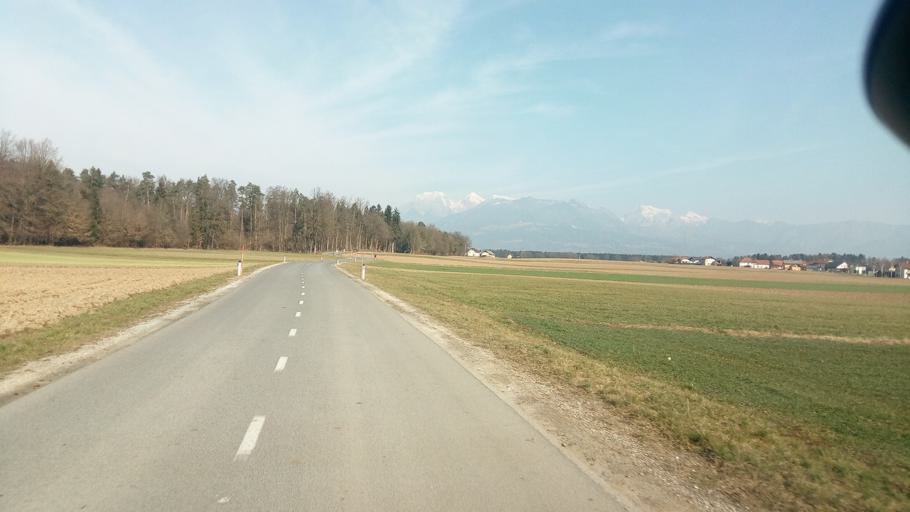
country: SI
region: Vodice
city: Vodice
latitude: 46.1591
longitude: 14.4862
